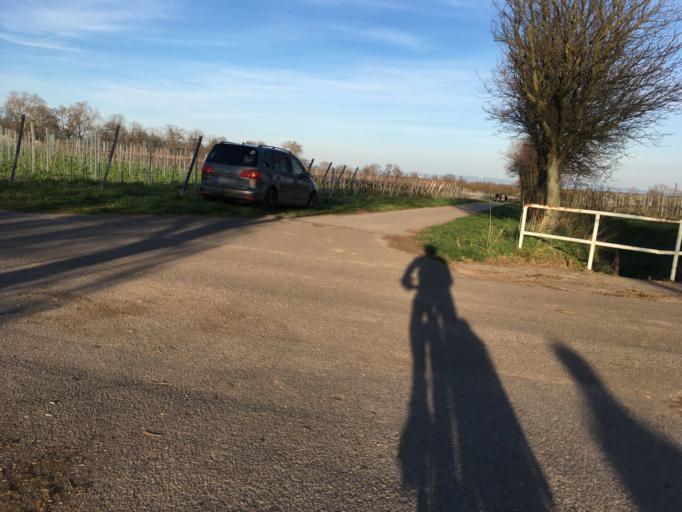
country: DE
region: Rheinland-Pfalz
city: Deidesheim
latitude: 49.3815
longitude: 8.1650
